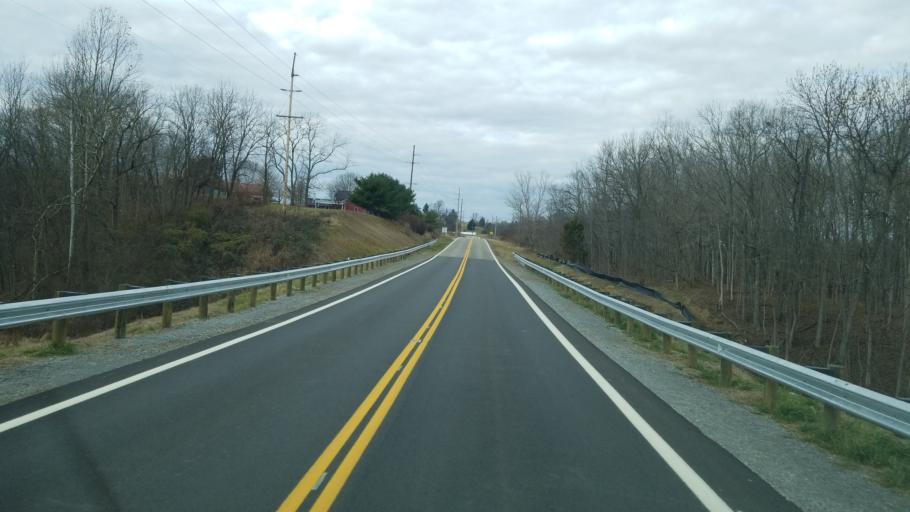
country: US
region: Ohio
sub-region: Ross County
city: Frankfort
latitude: 39.3517
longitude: -83.2302
